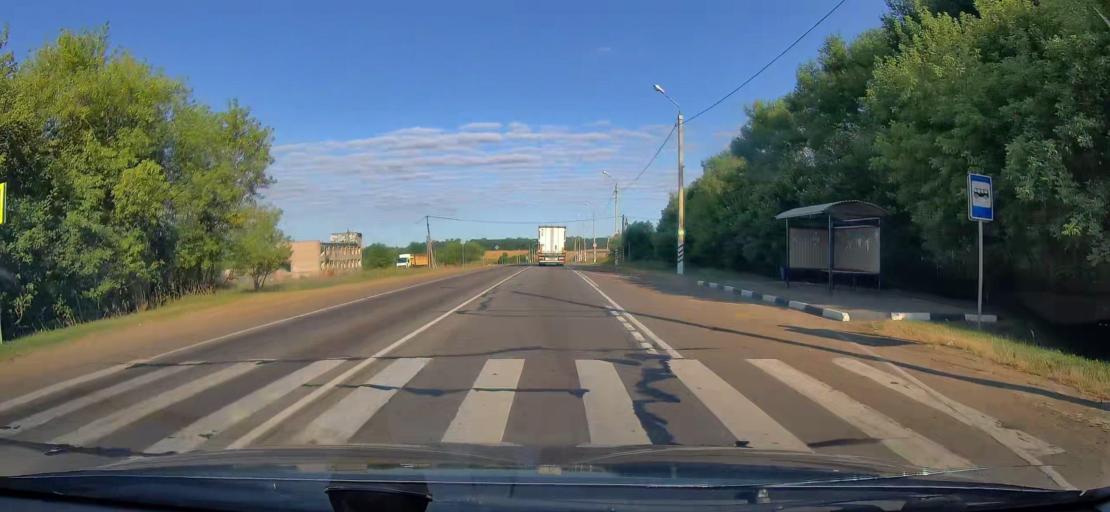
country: RU
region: Tula
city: Bol'shoye Skuratovo
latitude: 53.4536
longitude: 36.8748
